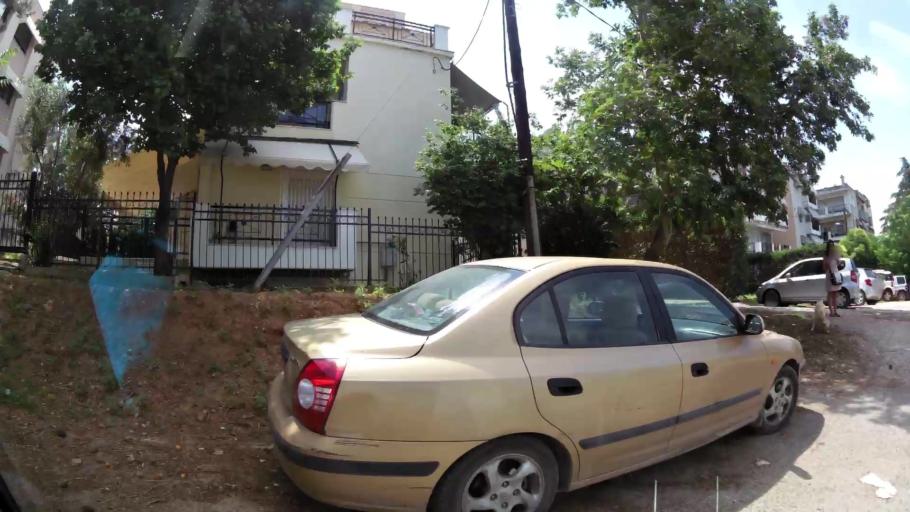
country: GR
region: Central Macedonia
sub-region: Nomos Thessalonikis
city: Pylaia
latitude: 40.6083
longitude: 22.9946
